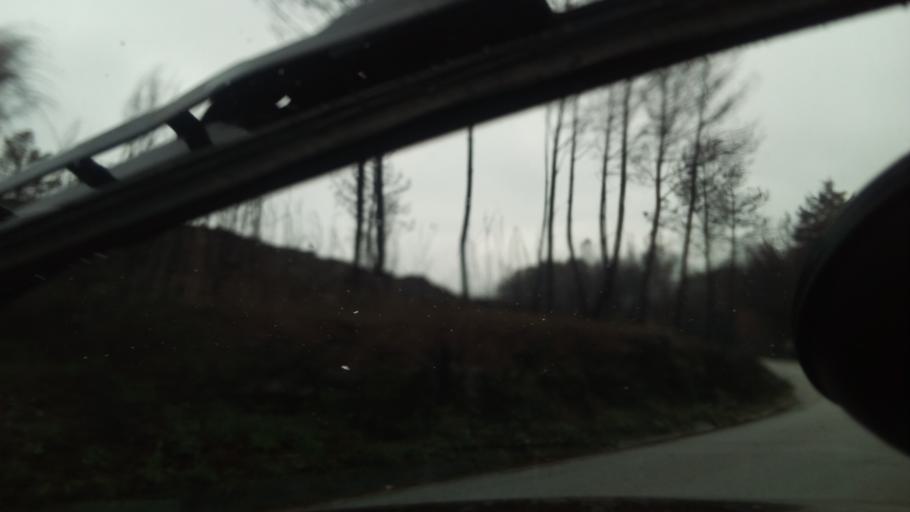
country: PT
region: Viseu
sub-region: Mangualde
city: Mangualde
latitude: 40.6126
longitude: -7.7881
